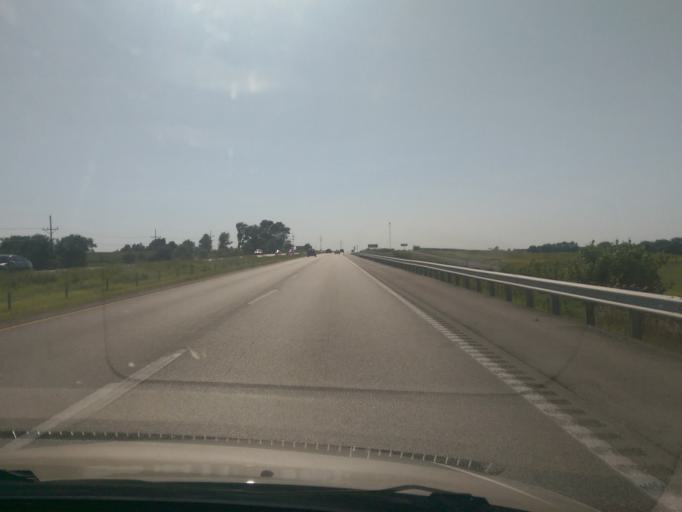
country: US
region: Missouri
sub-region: Saline County
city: Sweet Springs
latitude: 38.9789
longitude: -93.4621
